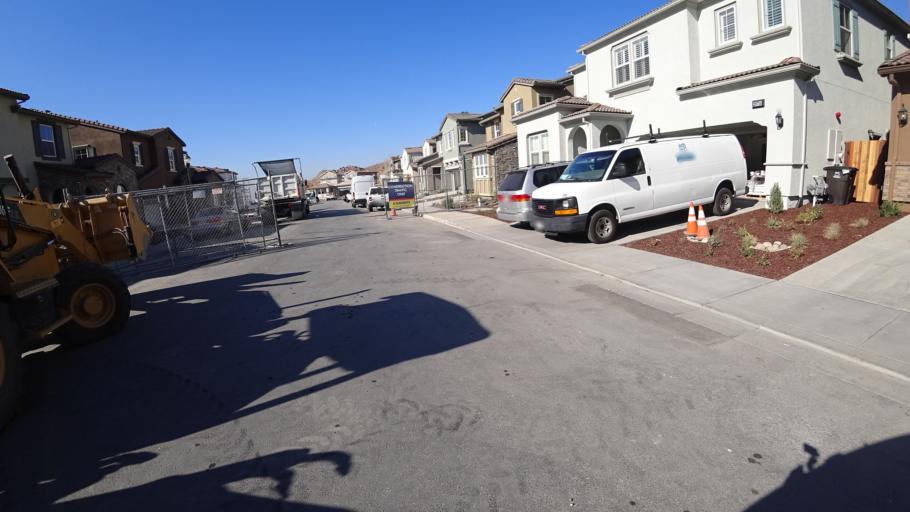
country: US
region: California
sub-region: Alameda County
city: Fairview
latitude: 37.6402
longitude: -122.0483
